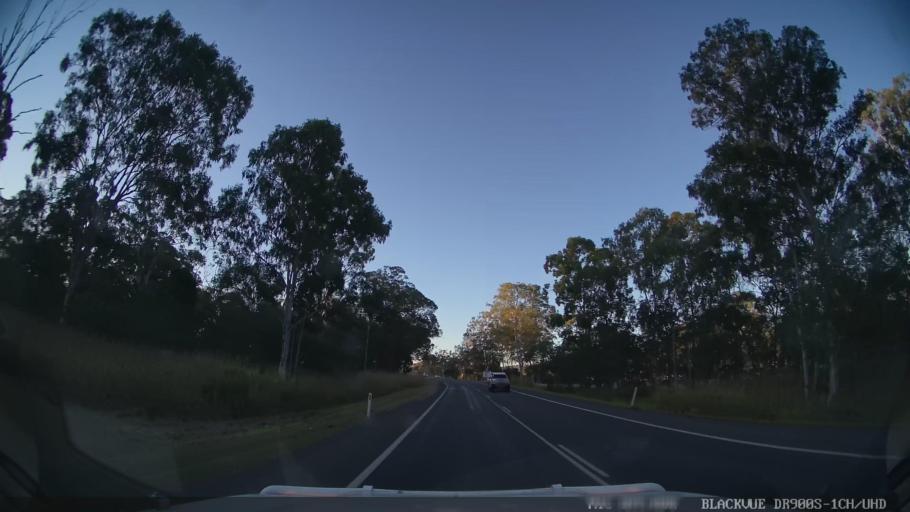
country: AU
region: Queensland
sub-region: Gladstone
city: Toolooa
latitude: -23.9570
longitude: 151.2198
